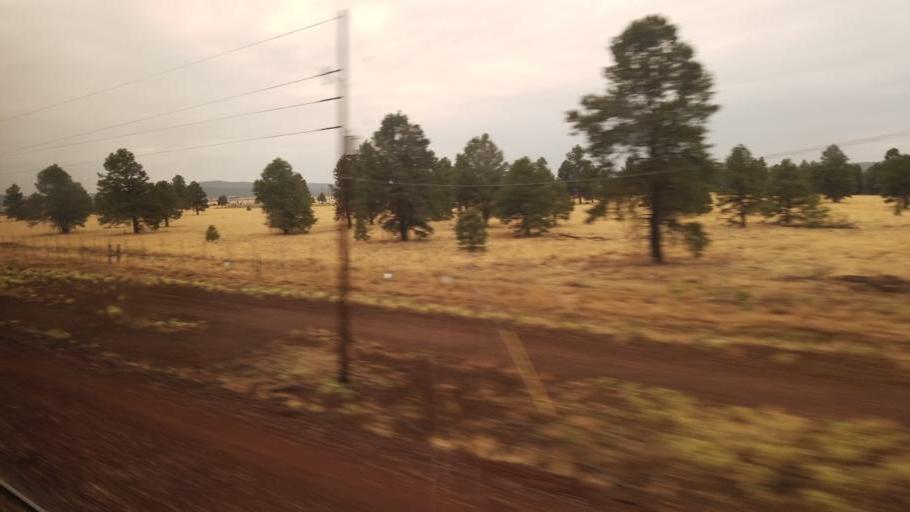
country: US
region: Arizona
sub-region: Coconino County
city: Parks
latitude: 35.2407
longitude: -111.8506
